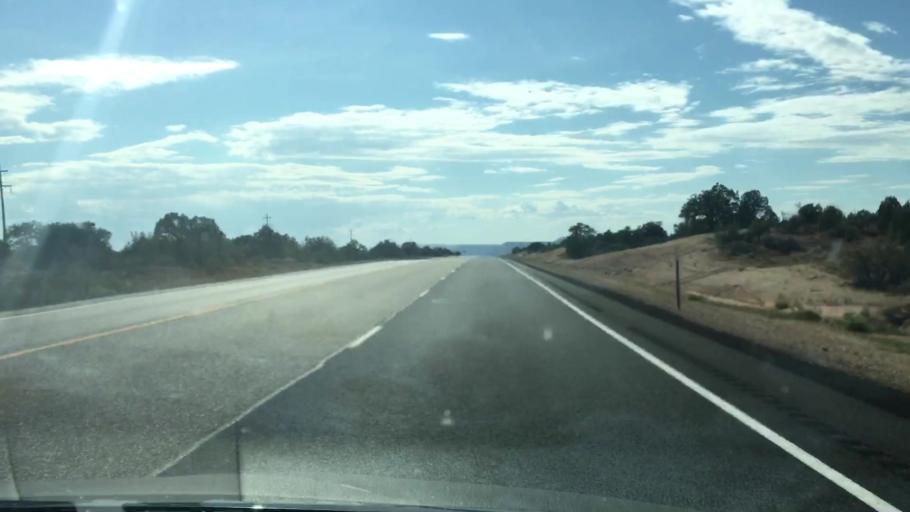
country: US
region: Utah
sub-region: Kane County
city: Kanab
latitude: 37.0414
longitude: -112.2291
